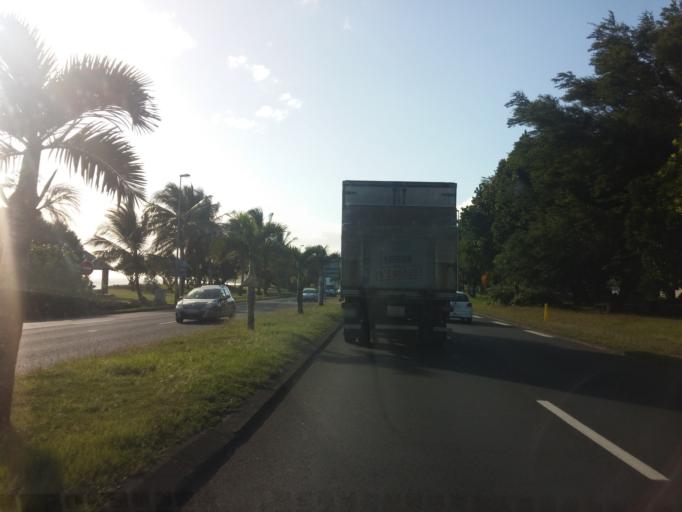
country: RE
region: Reunion
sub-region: Reunion
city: Saint-Denis
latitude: -20.8865
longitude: 55.4843
